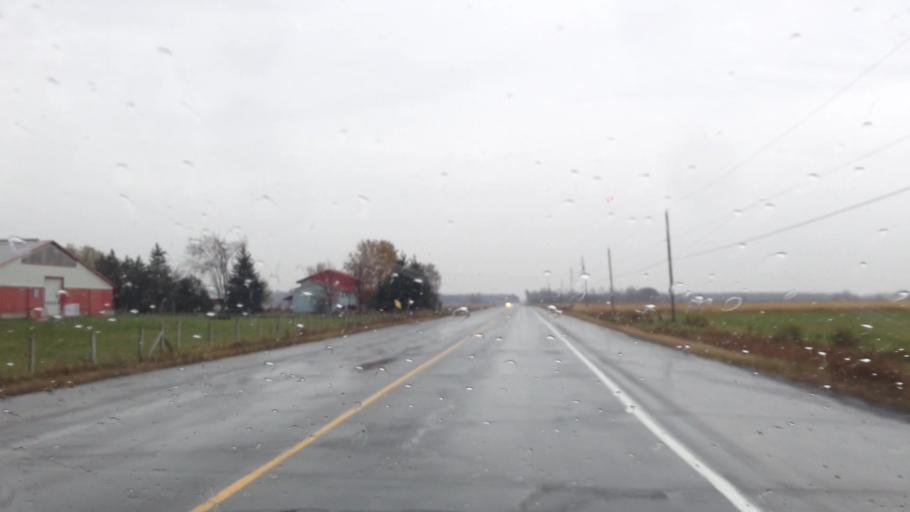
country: CA
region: Ontario
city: Clarence-Rockland
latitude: 45.4512
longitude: -75.4244
